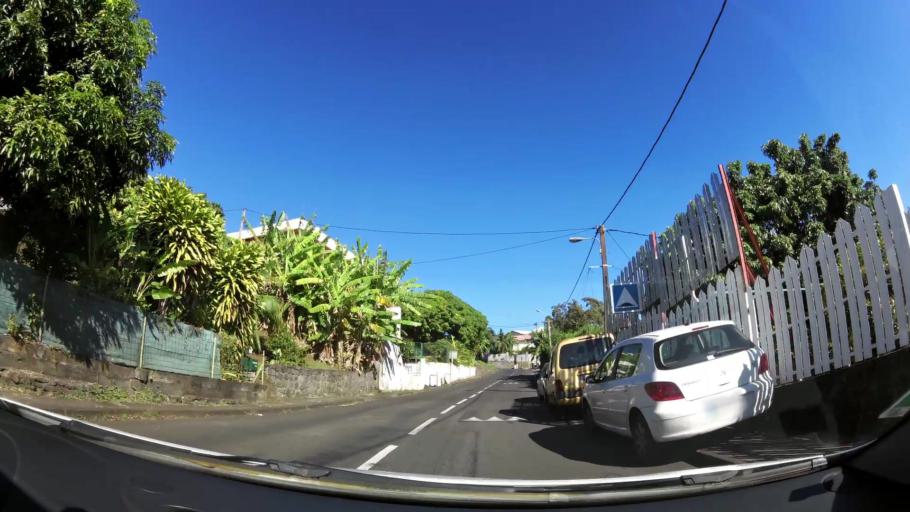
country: RE
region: Reunion
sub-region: Reunion
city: Saint-Denis
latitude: -20.9183
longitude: 55.4753
